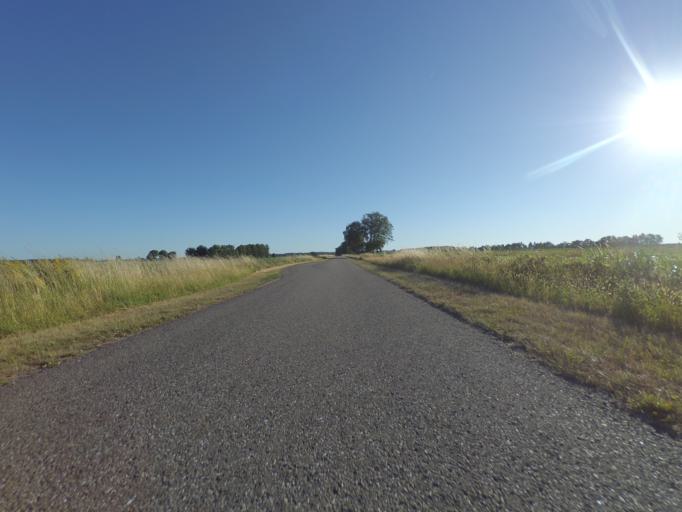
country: NL
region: North Holland
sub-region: Gemeente Wijdemeren
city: Nieuw-Loosdrecht
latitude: 52.1595
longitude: 5.1547
